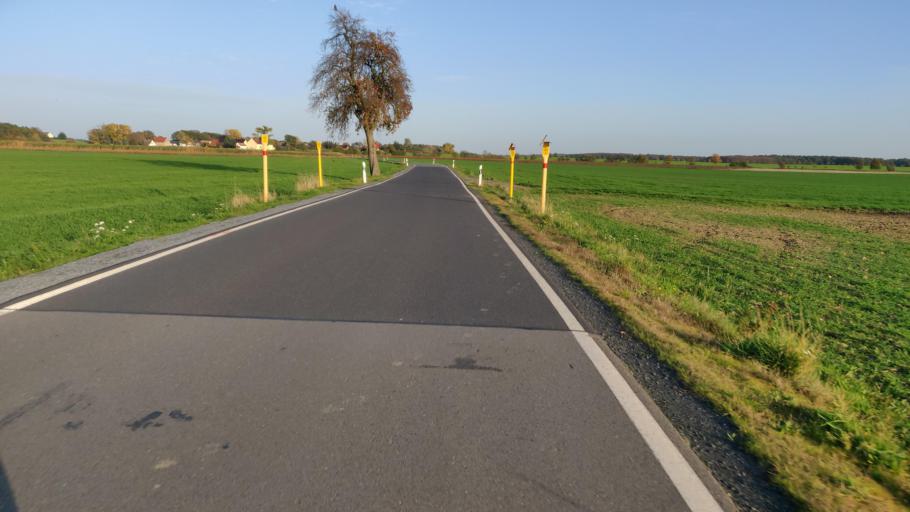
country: DE
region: Brandenburg
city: Hirschfeld
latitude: 51.3452
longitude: 13.6126
